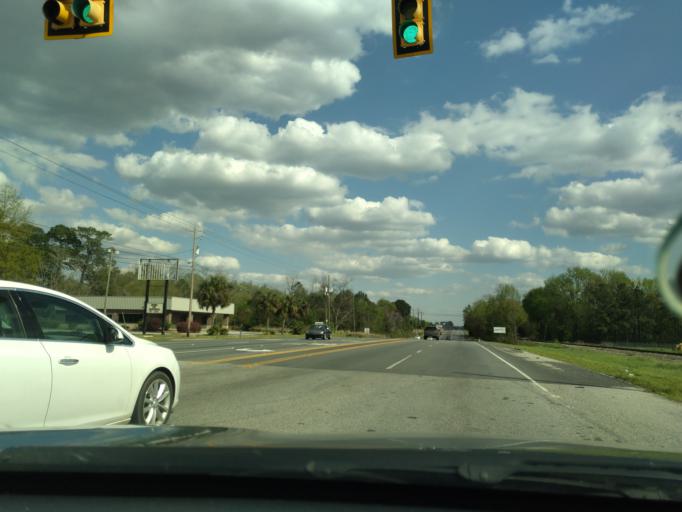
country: US
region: South Carolina
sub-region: Florence County
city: Florence
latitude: 34.2218
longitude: -79.7898
